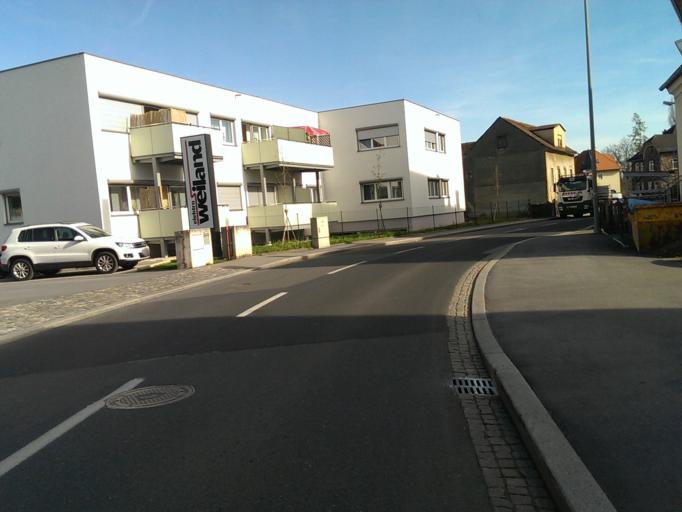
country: AT
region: Styria
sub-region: Graz Stadt
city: Graz
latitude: 47.0458
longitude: 15.4529
